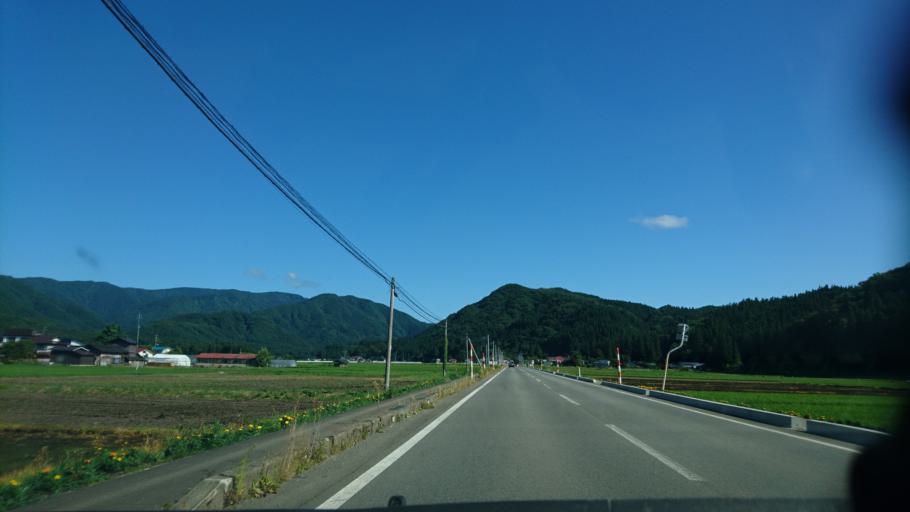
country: JP
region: Akita
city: Kakunodatemachi
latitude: 39.6713
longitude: 140.5670
